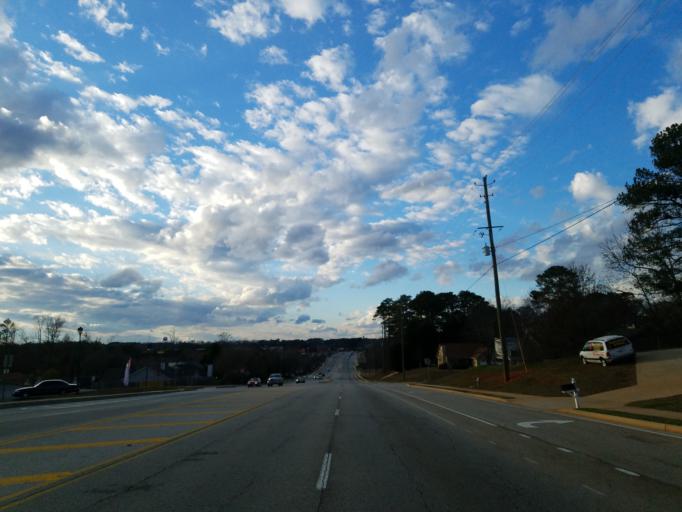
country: US
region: Georgia
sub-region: Henry County
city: McDonough
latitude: 33.4496
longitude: -84.1603
